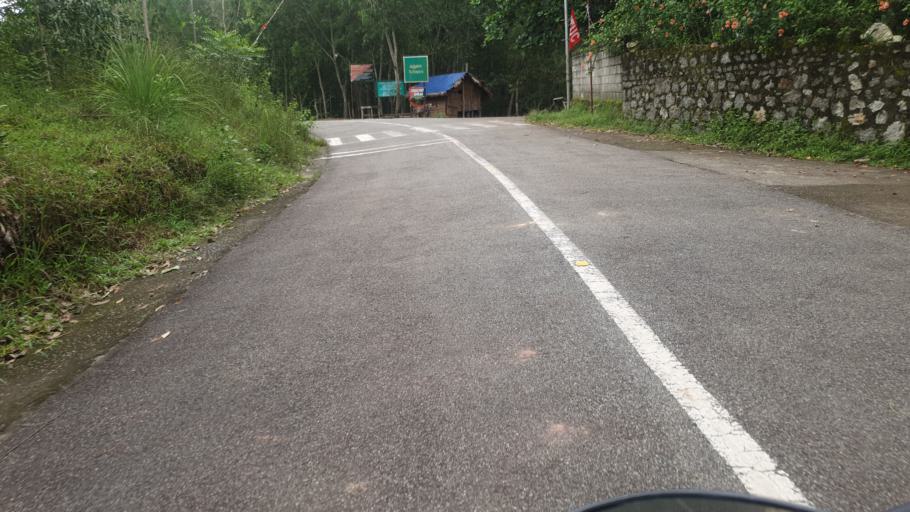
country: IN
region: Kerala
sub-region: Thiruvananthapuram
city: Nedumangad
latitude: 8.6342
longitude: 77.1120
